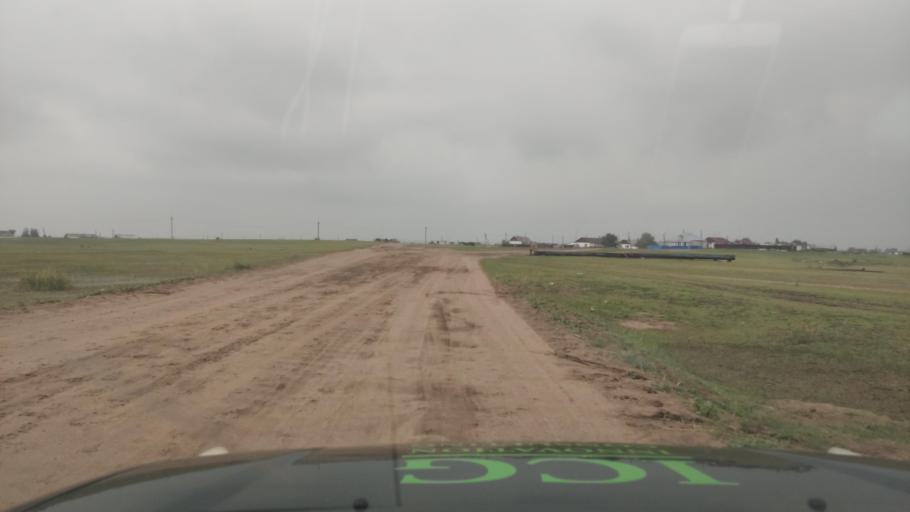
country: KZ
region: Pavlodar
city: Aksu
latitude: 52.0542
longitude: 77.1425
